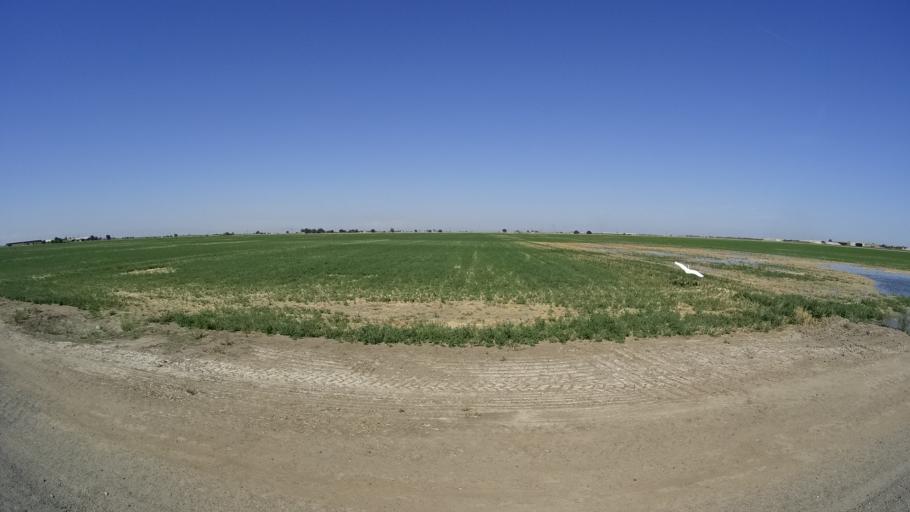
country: US
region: California
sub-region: Kings County
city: Home Garden
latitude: 36.2325
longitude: -119.5472
